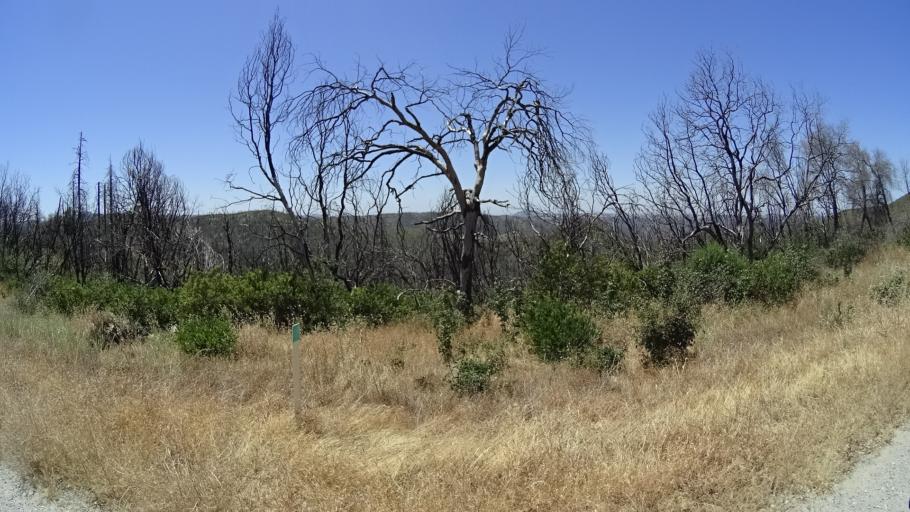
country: US
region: California
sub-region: Calaveras County
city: Mountain Ranch
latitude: 38.2814
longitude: -120.5962
